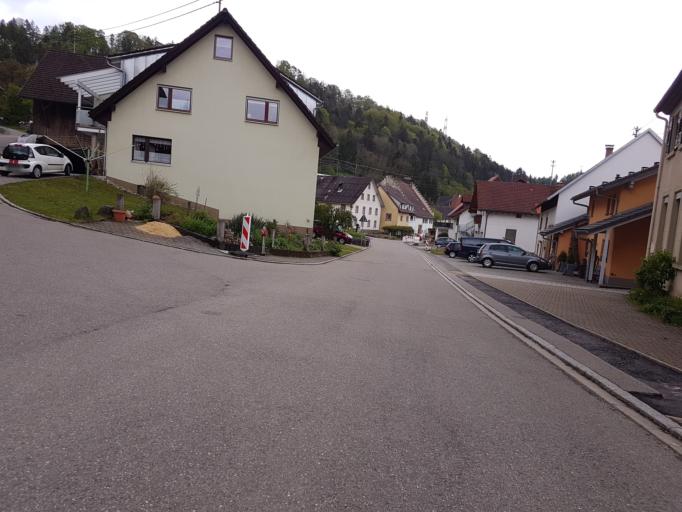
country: CH
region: Schaffhausen
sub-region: Bezirk Schleitheim
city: Schleitheim
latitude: 47.7866
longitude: 8.4966
